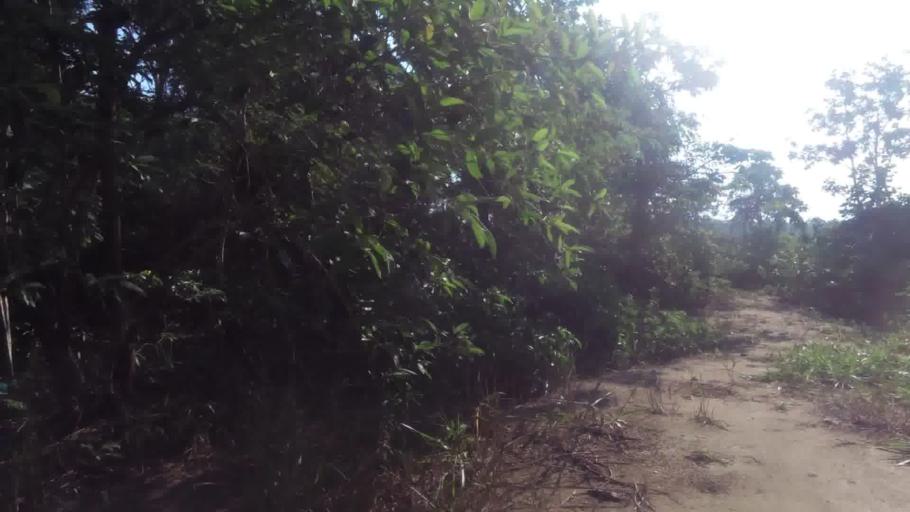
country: BR
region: Espirito Santo
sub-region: Piuma
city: Piuma
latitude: -20.8584
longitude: -40.7603
